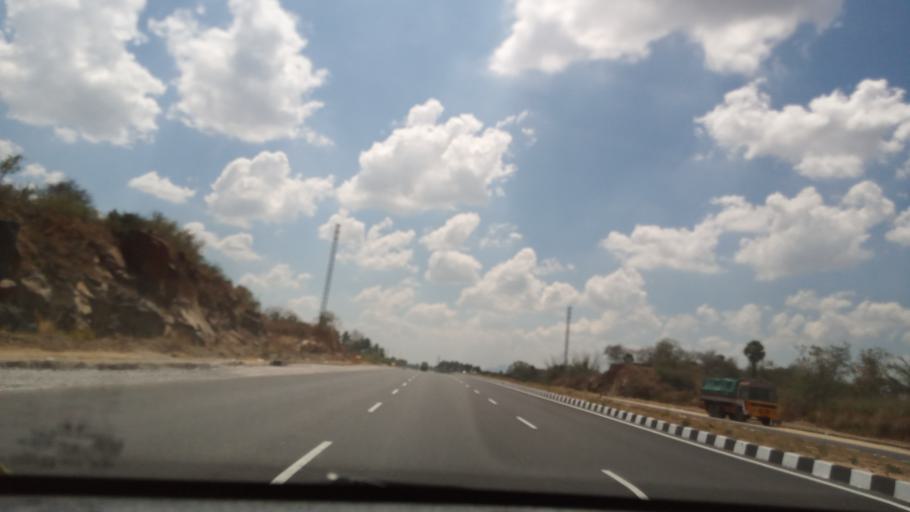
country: IN
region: Andhra Pradesh
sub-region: Chittoor
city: Pakala
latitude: 13.4497
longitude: 79.1565
